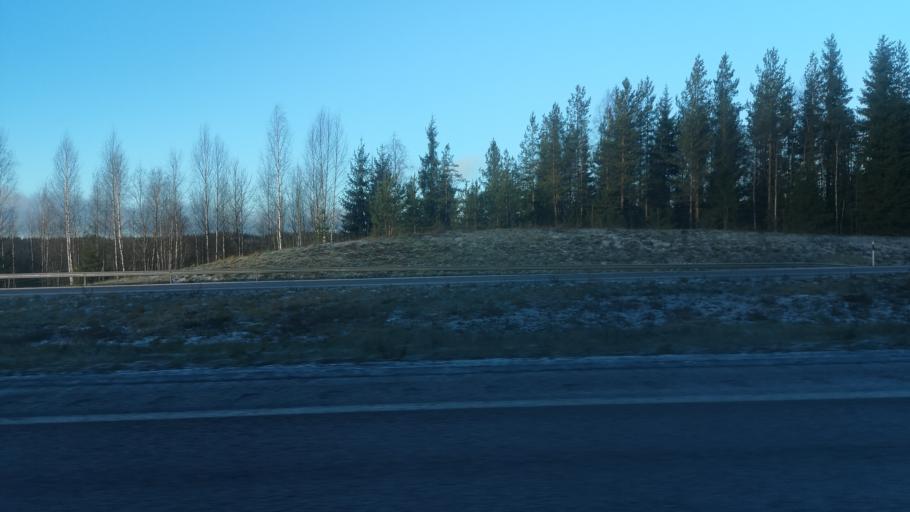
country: FI
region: Paijanne Tavastia
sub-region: Lahti
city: Nastola
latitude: 61.0318
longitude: 25.8400
